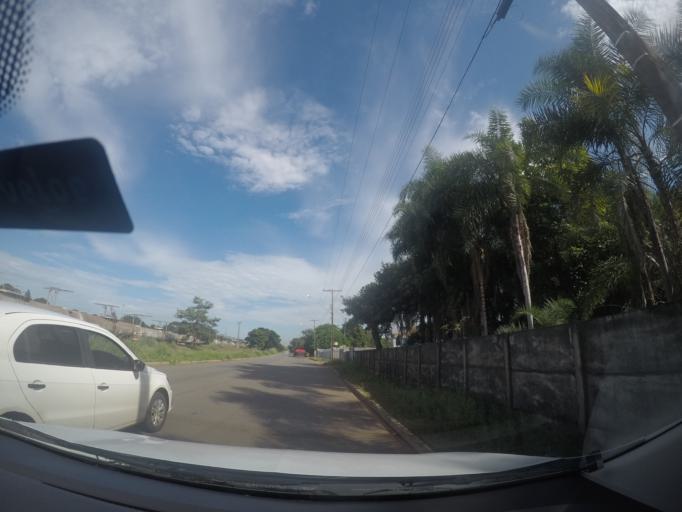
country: BR
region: Goias
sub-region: Goiania
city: Goiania
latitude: -16.6678
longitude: -49.2025
